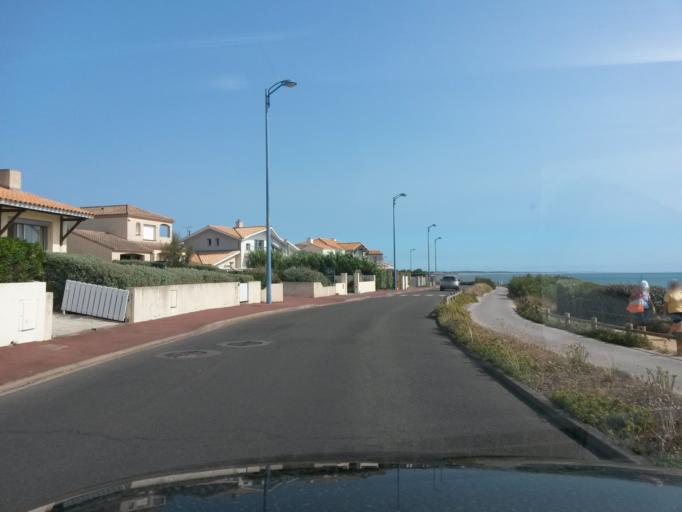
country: FR
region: Pays de la Loire
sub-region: Departement de la Vendee
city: Bretignolles-sur-Mer
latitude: 46.6341
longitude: -1.8876
